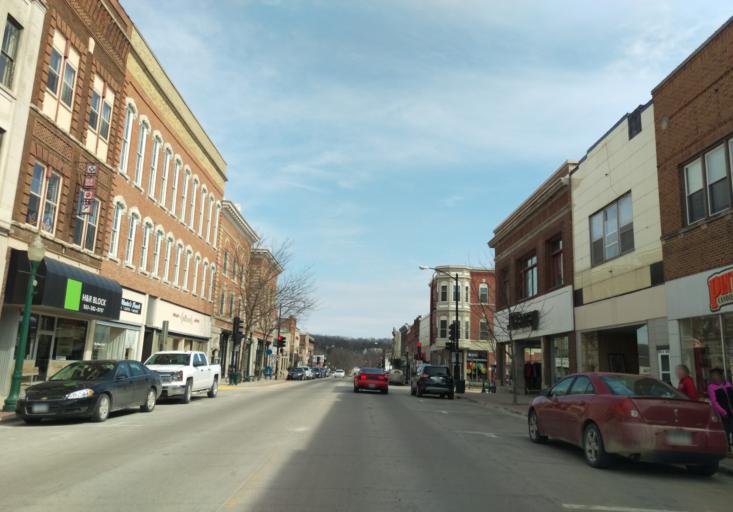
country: US
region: Iowa
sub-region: Winneshiek County
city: Decorah
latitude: 43.3041
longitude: -91.7865
